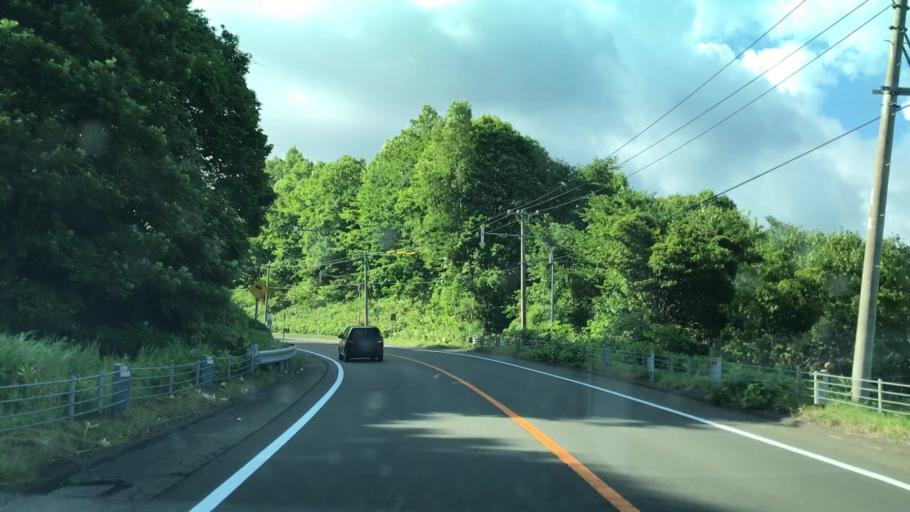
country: JP
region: Hokkaido
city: Shimo-furano
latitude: 42.9081
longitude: 142.4177
